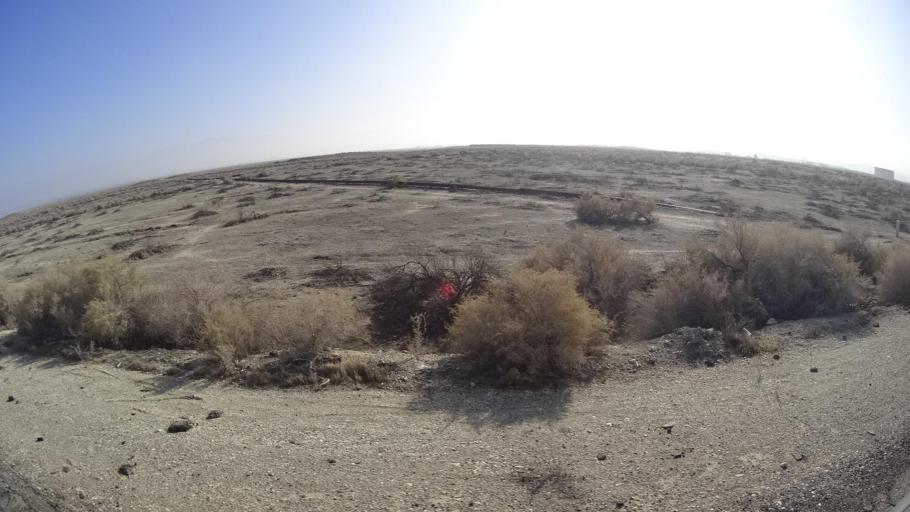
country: US
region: California
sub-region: Kern County
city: Maricopa
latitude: 35.1010
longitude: -119.3869
